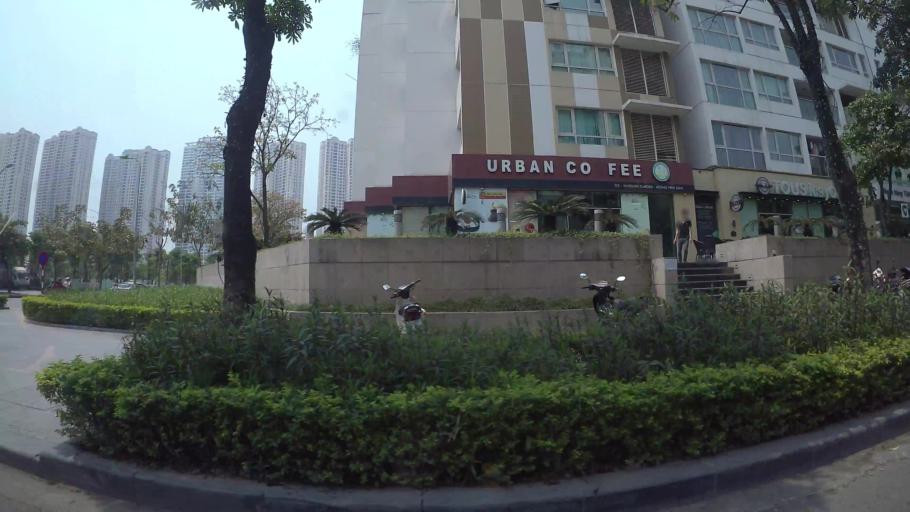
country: VN
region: Ha Noi
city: Thanh Xuan
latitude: 21.0042
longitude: 105.7991
